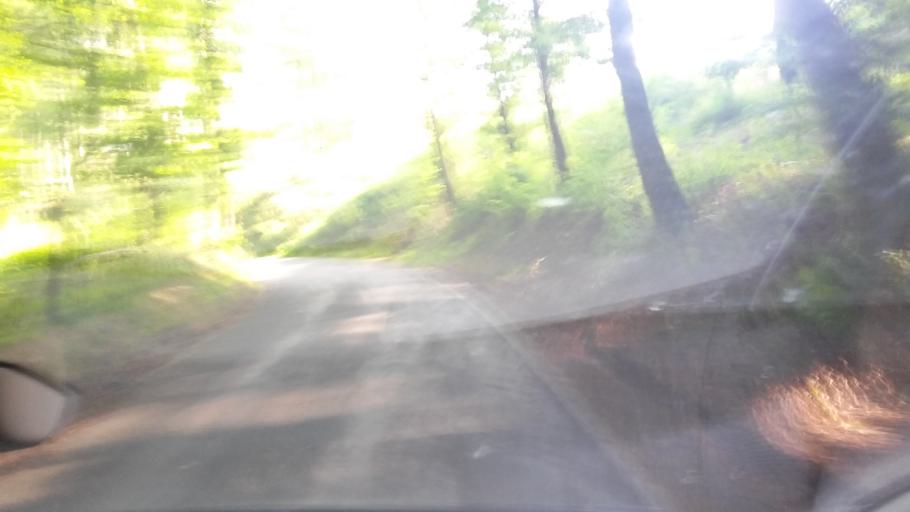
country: LU
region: Luxembourg
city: Eischen
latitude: 49.7061
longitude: 5.8632
